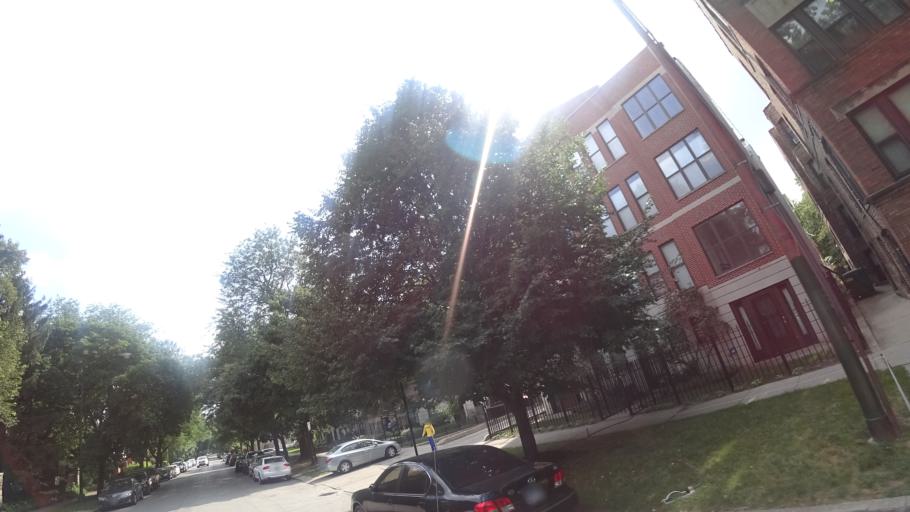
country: US
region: Illinois
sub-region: Cook County
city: Chicago
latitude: 41.8091
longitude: -87.5969
